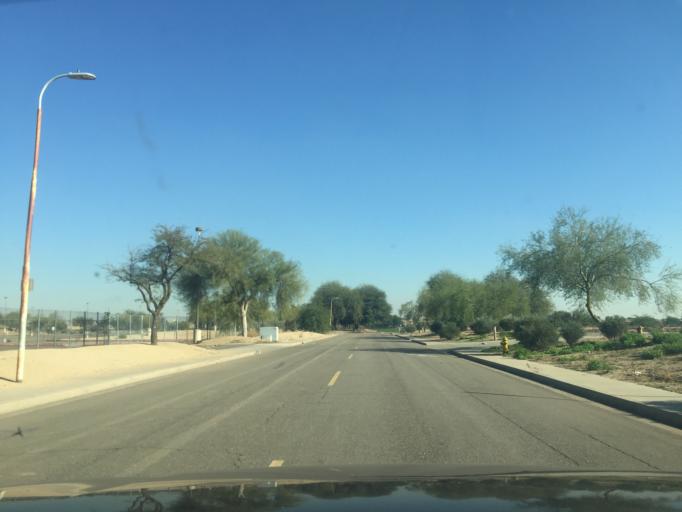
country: US
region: Arizona
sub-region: Maricopa County
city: Tolleson
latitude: 33.4690
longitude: -112.2352
